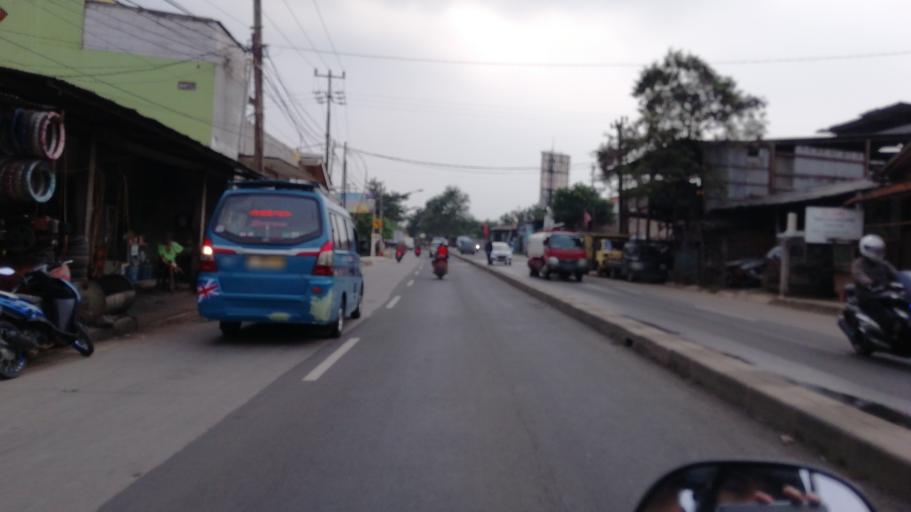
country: ID
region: West Java
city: Parung
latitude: -6.4833
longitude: 106.7323
